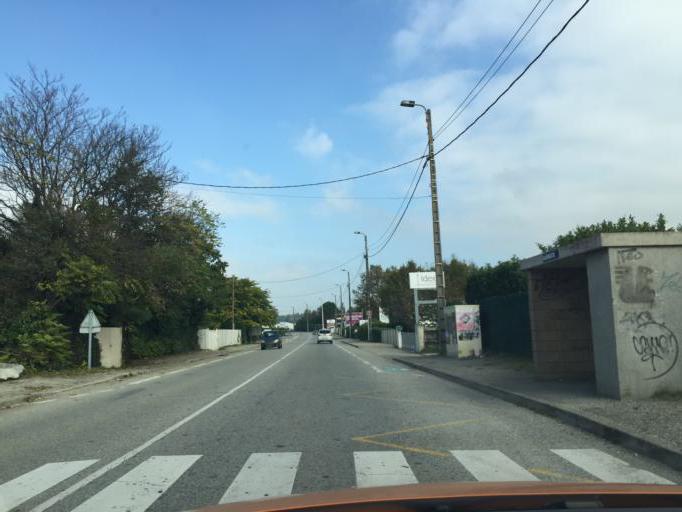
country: FR
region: Rhone-Alpes
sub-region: Departement de la Drome
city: Portes-les-Valence
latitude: 44.8797
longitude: 4.8864
